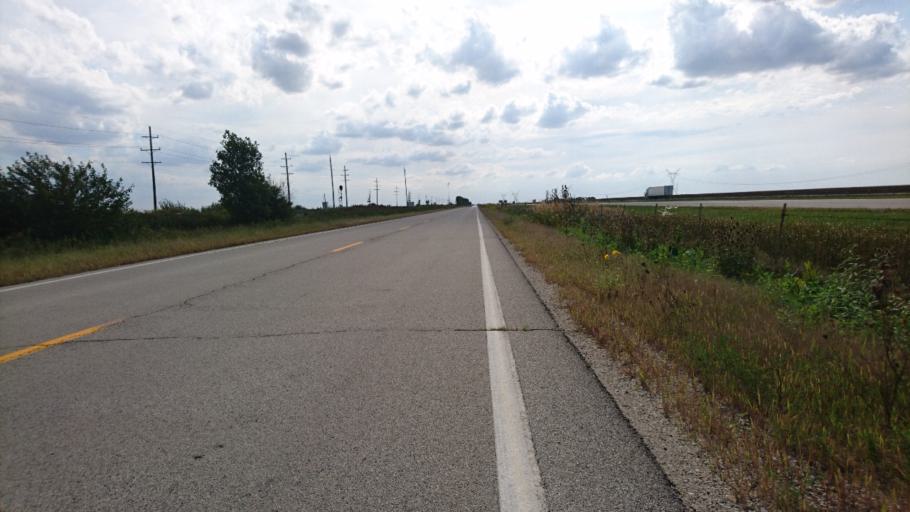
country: US
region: Illinois
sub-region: Grundy County
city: Gardner
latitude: 41.1501
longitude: -88.3561
